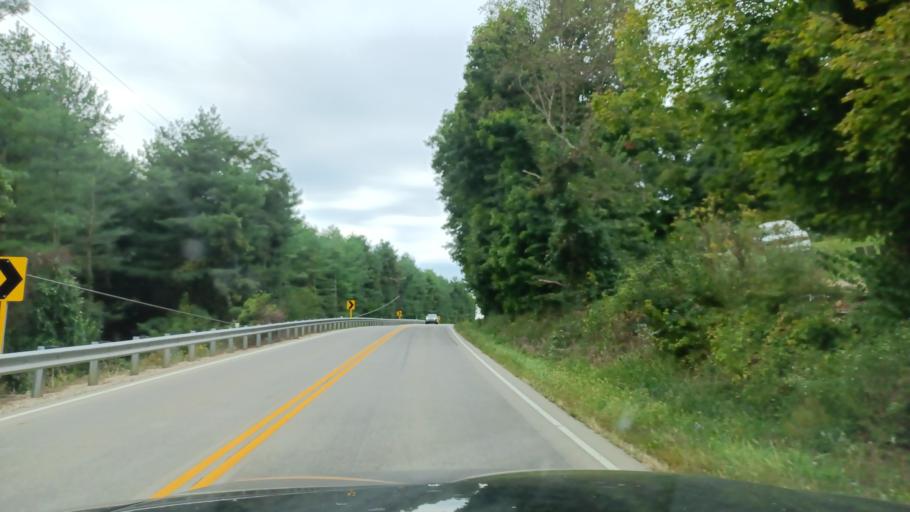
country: US
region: Ohio
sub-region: Ross County
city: Chillicothe
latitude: 39.2843
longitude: -82.8608
